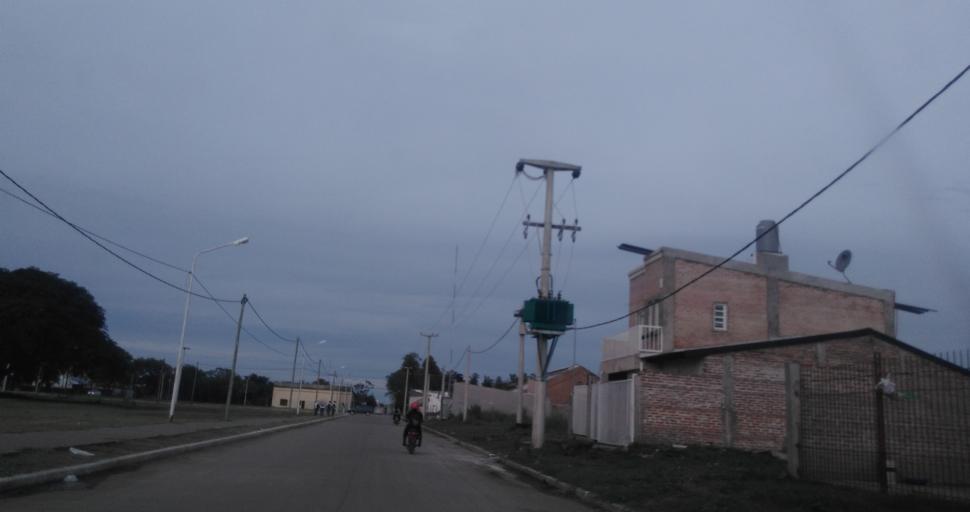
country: AR
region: Chaco
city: Fontana
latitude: -27.4181
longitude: -59.0346
